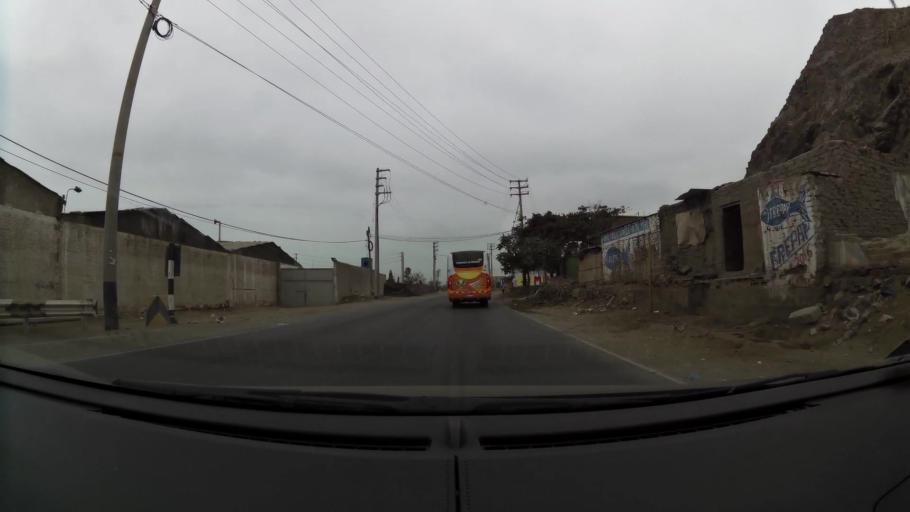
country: PE
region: Ancash
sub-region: Provincia de Santa
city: Coishco
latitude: -9.0154
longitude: -78.6191
